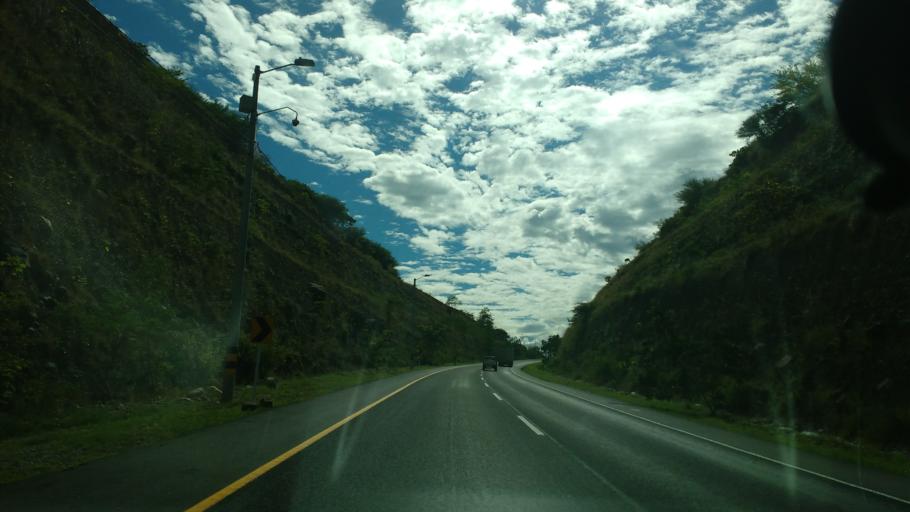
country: CO
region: Tolima
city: Valle de San Juan
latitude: 4.2930
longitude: -75.0399
